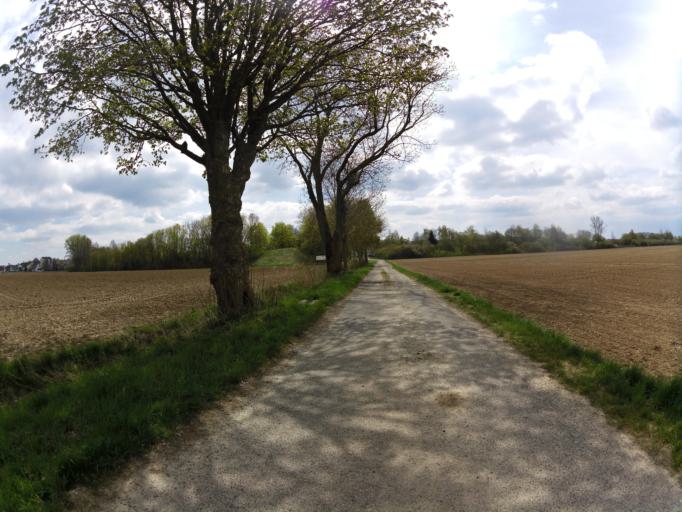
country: DE
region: Bavaria
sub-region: Regierungsbezirk Unterfranken
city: Giebelstadt
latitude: 49.6586
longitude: 9.9373
